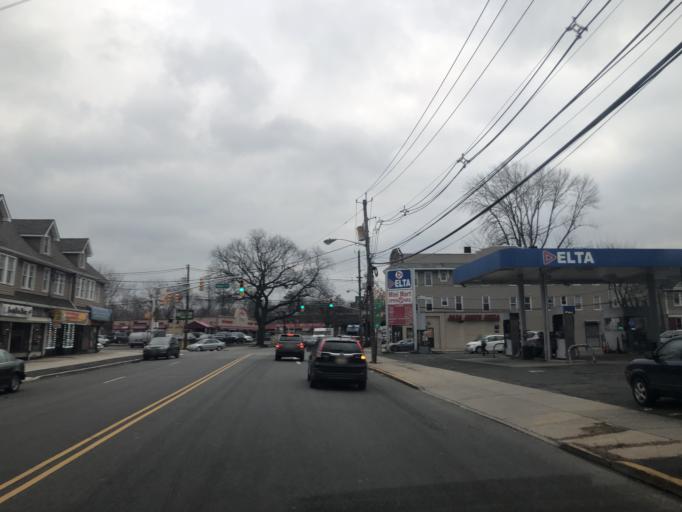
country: US
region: New Jersey
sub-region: Essex County
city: Irvington
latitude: 40.7222
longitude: -74.2340
